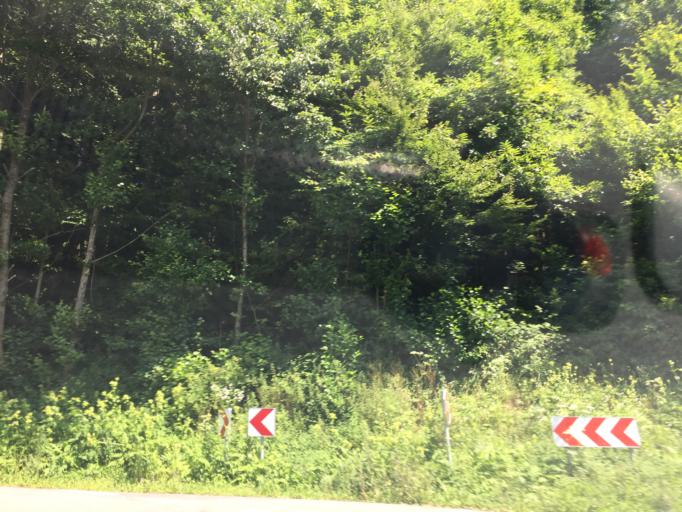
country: SI
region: Trbovlje
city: Trbovlje
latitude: 46.1834
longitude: 15.0585
